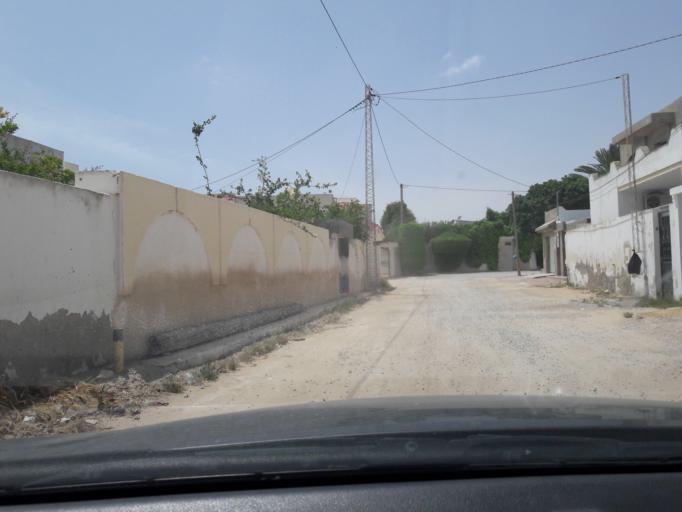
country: TN
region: Safaqis
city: Al Qarmadah
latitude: 34.7809
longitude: 10.7594
